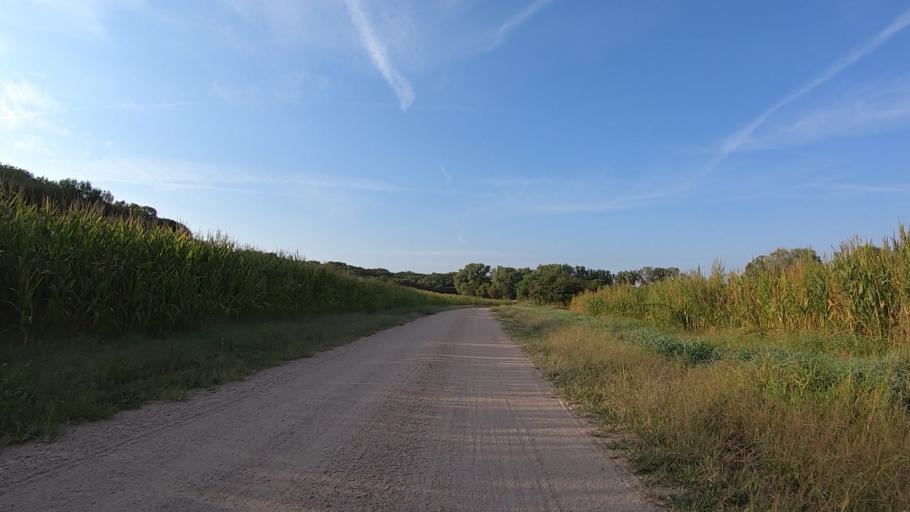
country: US
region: Kansas
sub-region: Marshall County
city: Blue Rapids
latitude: 39.7217
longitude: -96.7664
